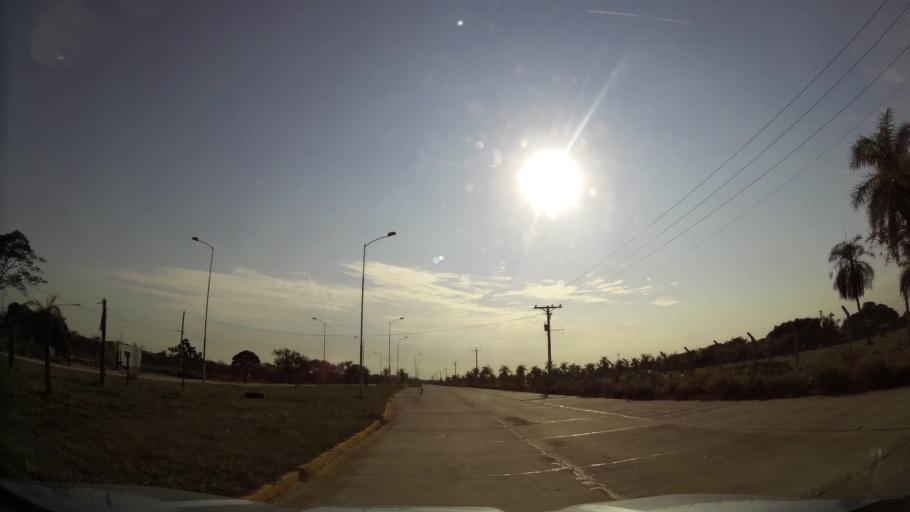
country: BO
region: Santa Cruz
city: Santa Cruz de la Sierra
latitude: -17.6979
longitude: -63.1242
